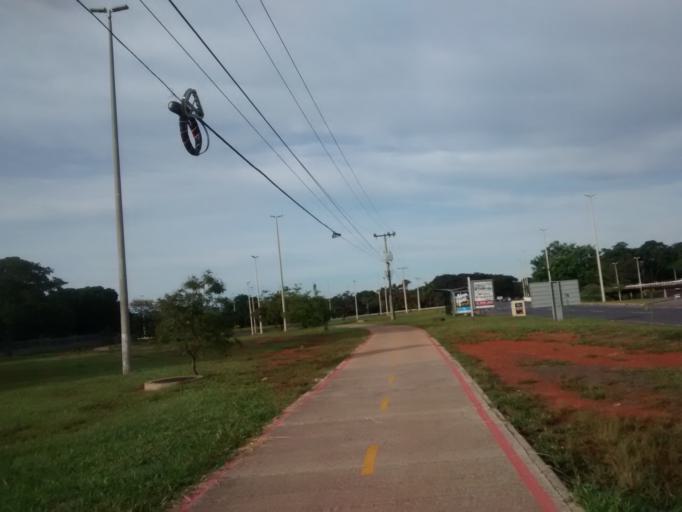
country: BR
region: Federal District
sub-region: Brasilia
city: Brasilia
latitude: -15.8009
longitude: -47.8767
